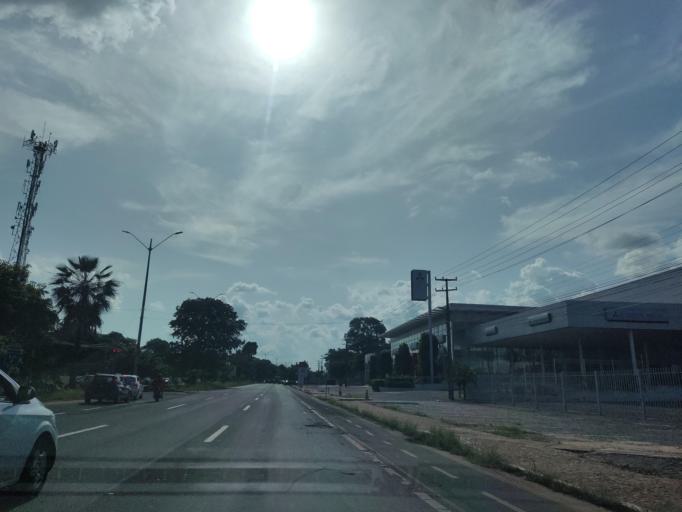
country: BR
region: Piaui
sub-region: Teresina
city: Teresina
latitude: -5.0814
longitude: -42.7672
